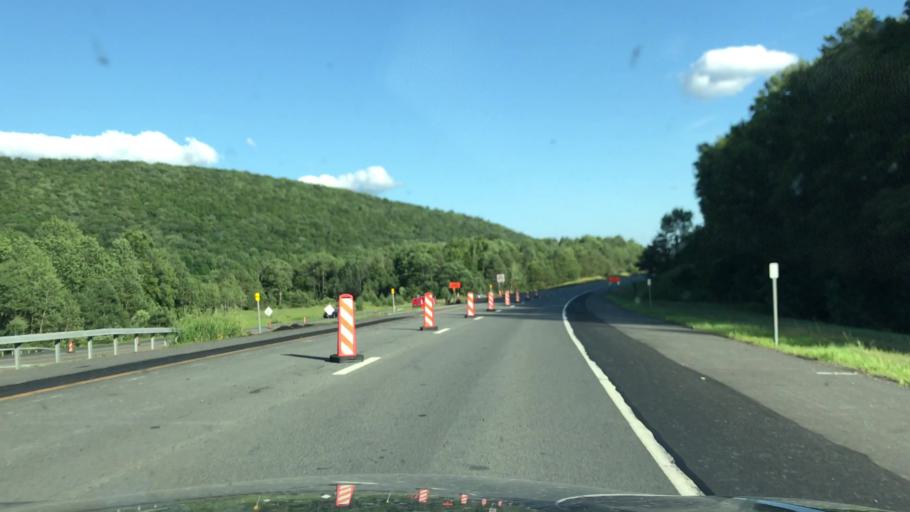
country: US
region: New York
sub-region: Sullivan County
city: Livingston Manor
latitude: 41.9550
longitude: -74.9355
